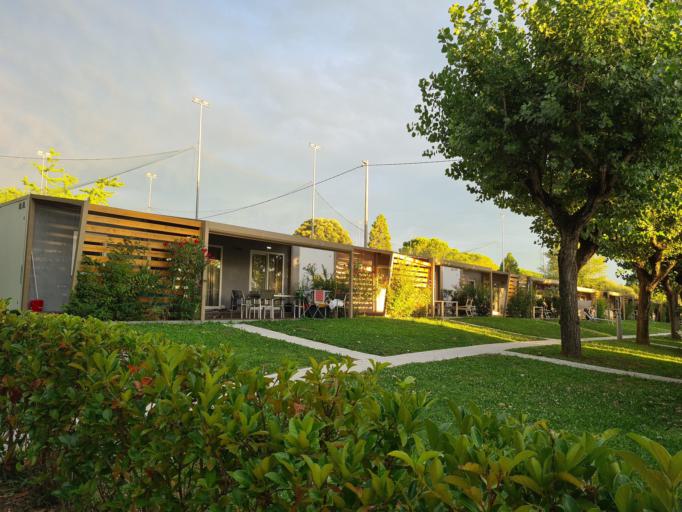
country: IT
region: Veneto
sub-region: Provincia di Verona
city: Lazise
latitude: 45.4928
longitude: 10.7339
